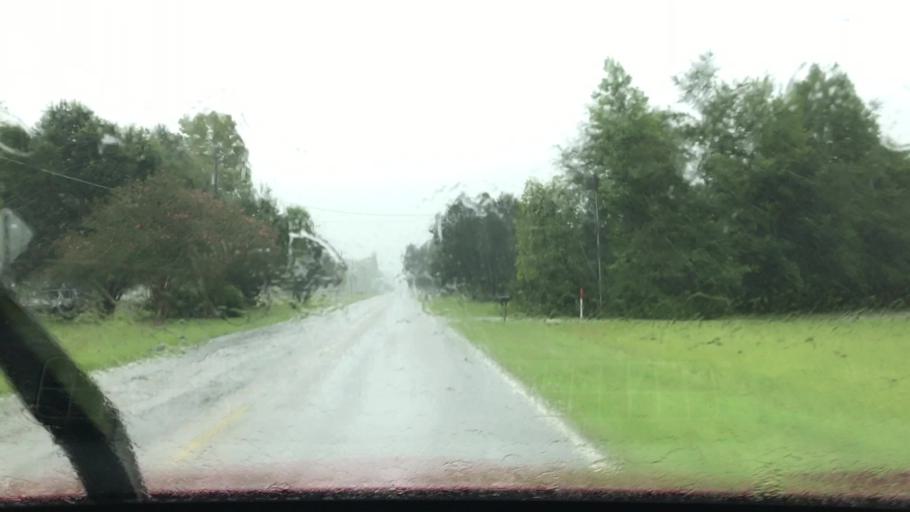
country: US
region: South Carolina
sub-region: Horry County
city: Red Hill
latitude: 33.8787
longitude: -78.9700
